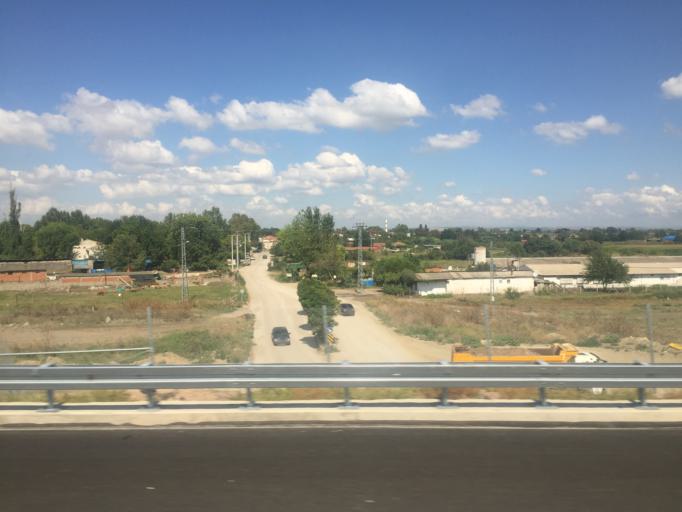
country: TR
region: Balikesir
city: Gobel
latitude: 40.0576
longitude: 28.2379
